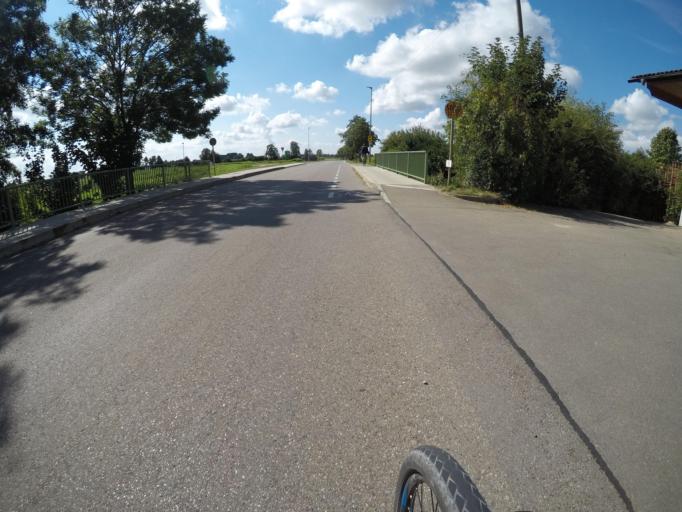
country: DE
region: Bavaria
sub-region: Swabia
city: Finningen
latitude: 48.6216
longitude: 10.5087
